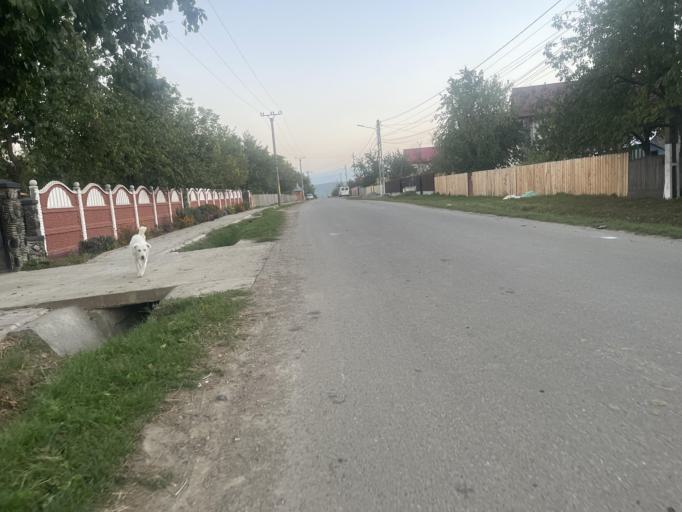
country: RO
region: Iasi
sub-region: Comuna Dumesti
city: Pausesti
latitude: 47.1525
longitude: 27.3236
